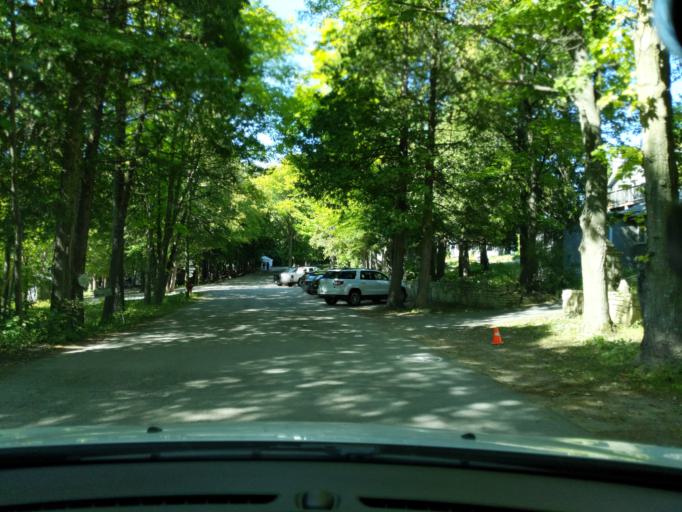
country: US
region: Wisconsin
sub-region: Door County
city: Sturgeon Bay
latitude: 45.1856
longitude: -87.1476
